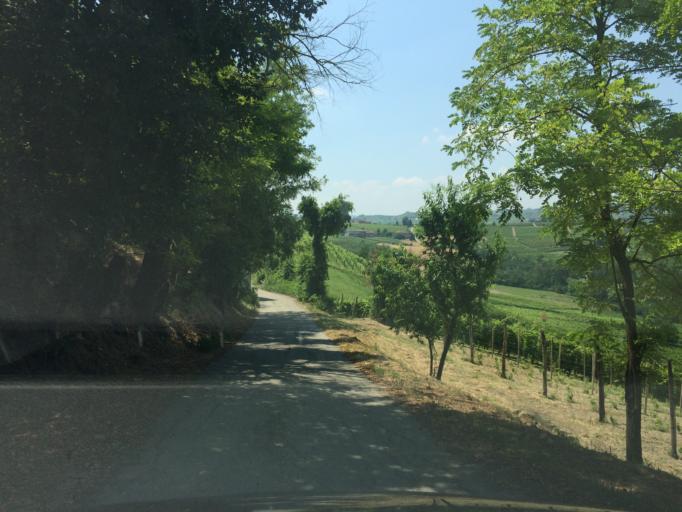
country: IT
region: Piedmont
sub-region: Provincia di Asti
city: Moasca
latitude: 44.7612
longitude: 8.2605
